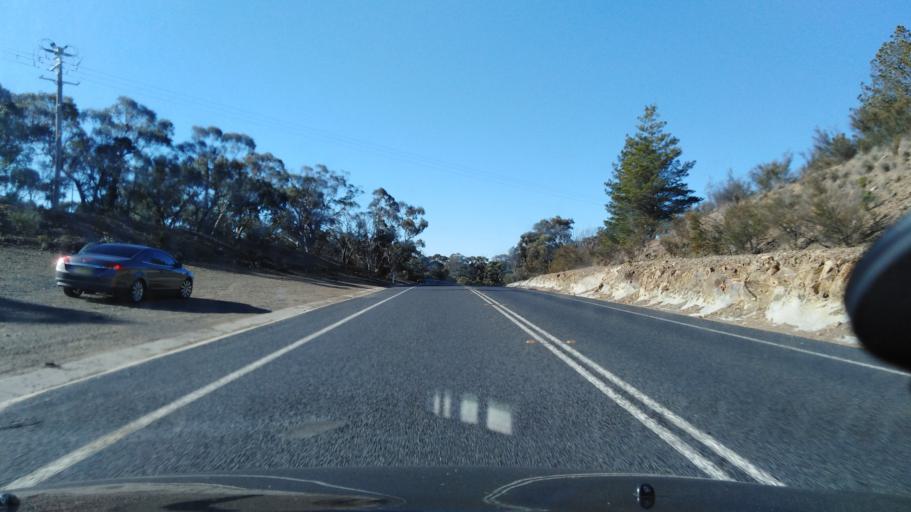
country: AU
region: New South Wales
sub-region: Palerang
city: Bungendore
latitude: -35.1861
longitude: 149.3126
